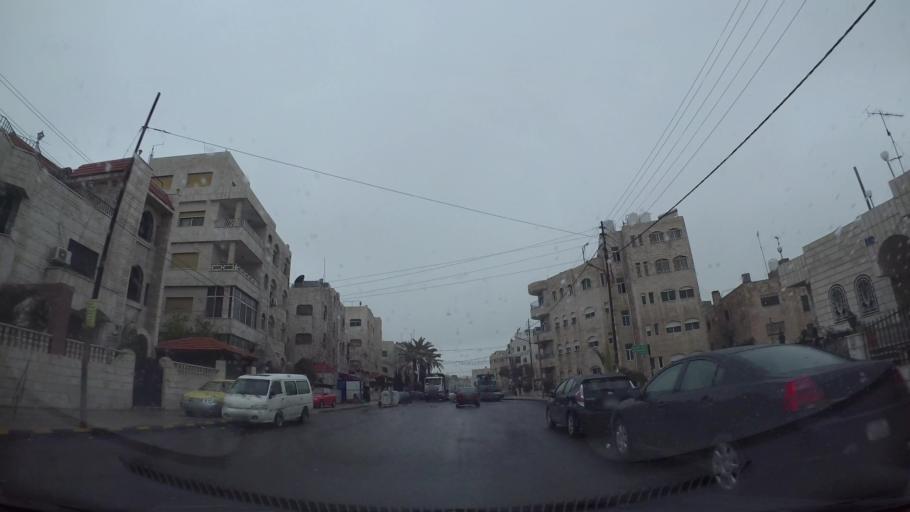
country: JO
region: Amman
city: Amman
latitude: 31.9767
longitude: 35.9166
